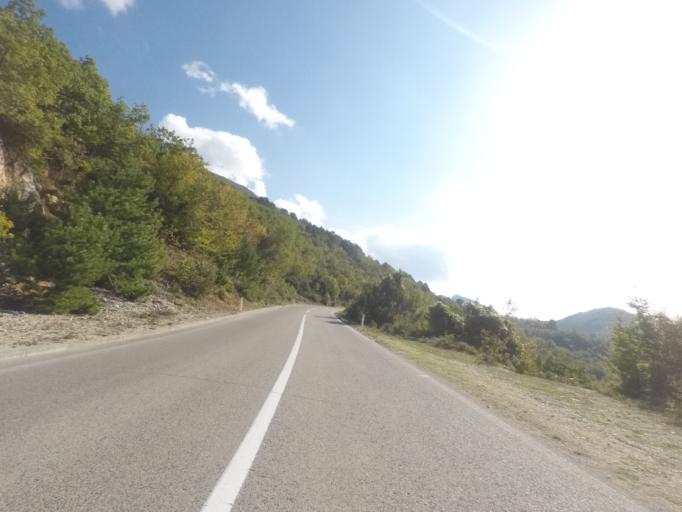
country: BA
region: Republika Srpska
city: Trebinje
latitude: 42.7154
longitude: 18.5211
